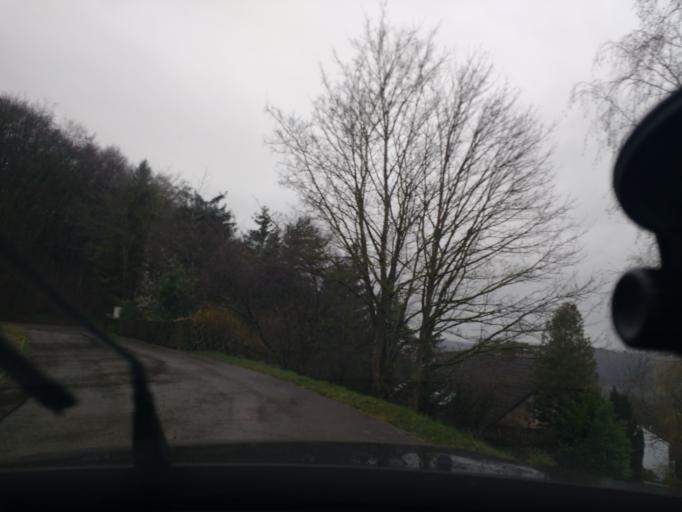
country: LU
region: Grevenmacher
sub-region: Canton de Grevenmacher
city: Grevenmacher
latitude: 49.6741
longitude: 6.4520
